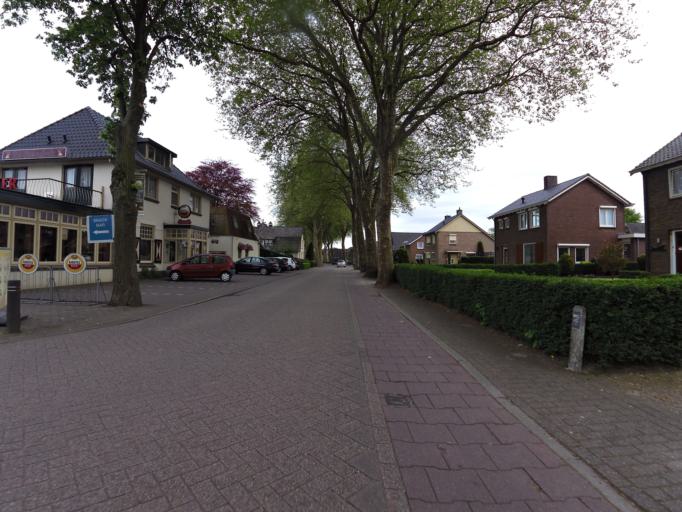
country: NL
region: Gelderland
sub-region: Gemeente Montferland
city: s-Heerenberg
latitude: 51.9061
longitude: 6.1908
